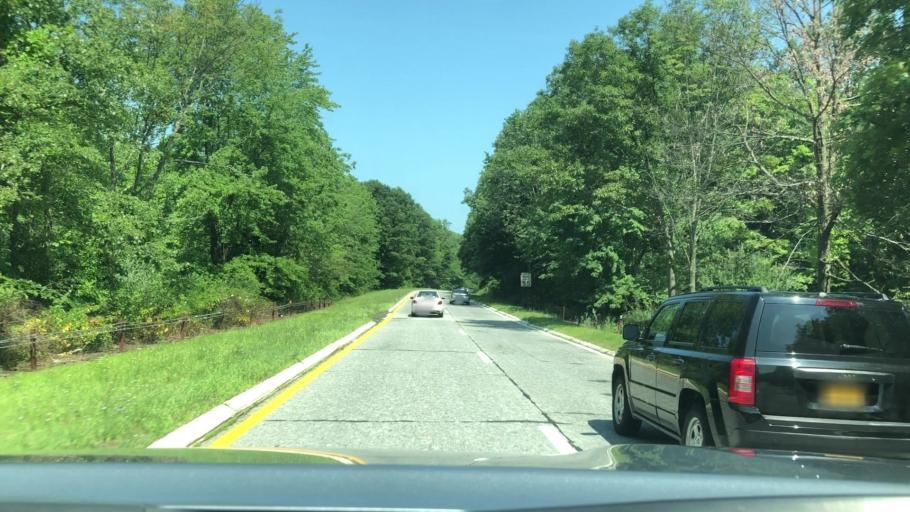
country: US
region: New York
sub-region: Rockland County
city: Stony Point
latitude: 41.2729
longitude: -74.0306
